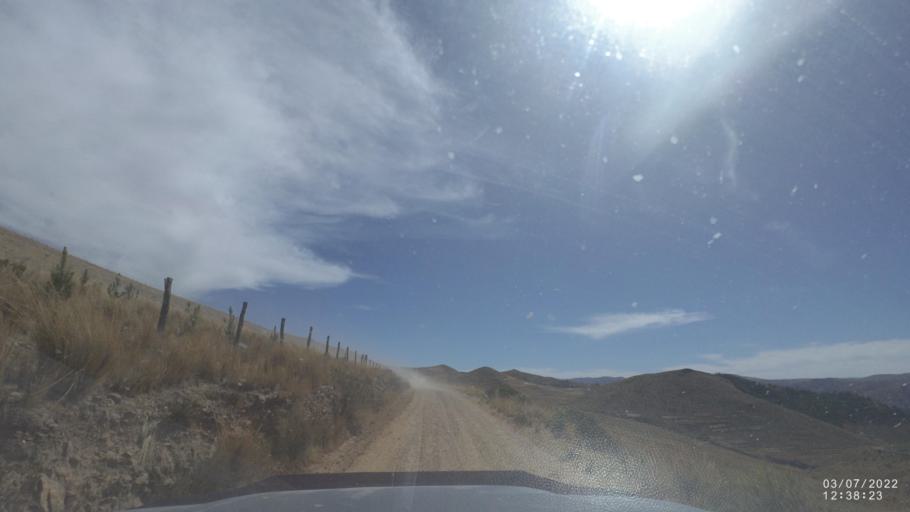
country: BO
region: Cochabamba
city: Irpa Irpa
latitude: -17.7926
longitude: -66.6189
